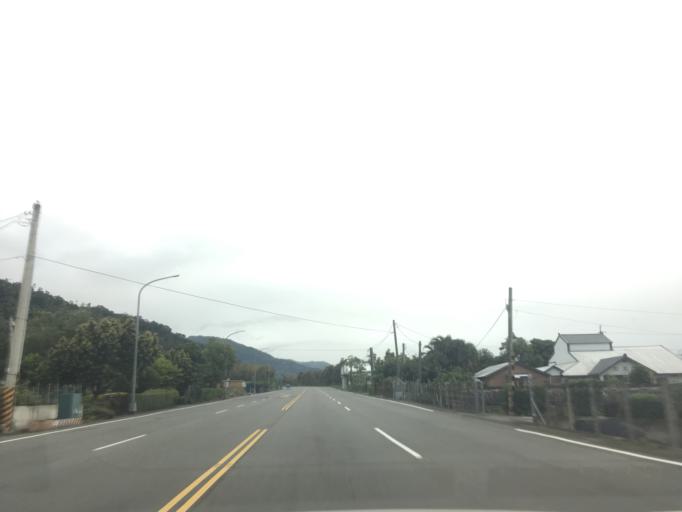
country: TW
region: Taiwan
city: Taitung City
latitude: 22.7333
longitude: 121.0563
